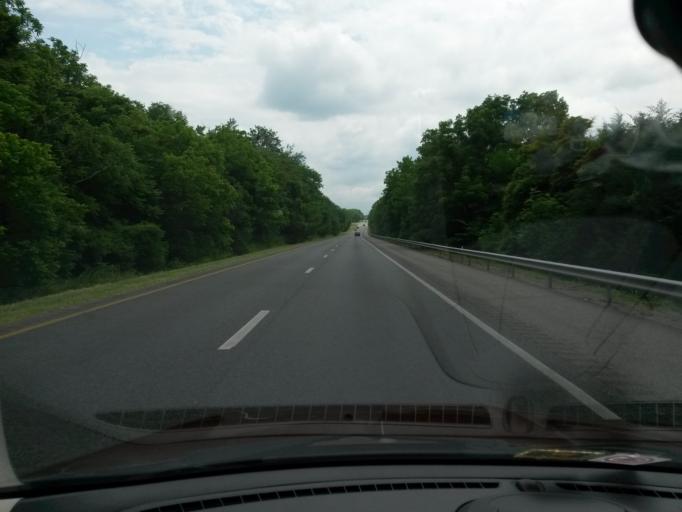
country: US
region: Virginia
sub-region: City of Charlottesville
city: Charlottesville
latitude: 38.0185
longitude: -78.4078
